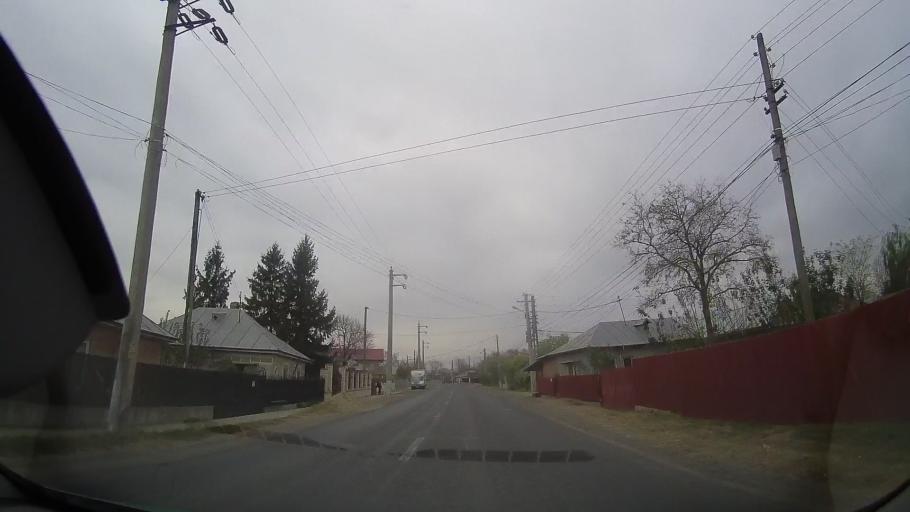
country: RO
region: Buzau
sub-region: Comuna Padina
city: Padina
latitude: 44.8224
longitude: 27.1158
